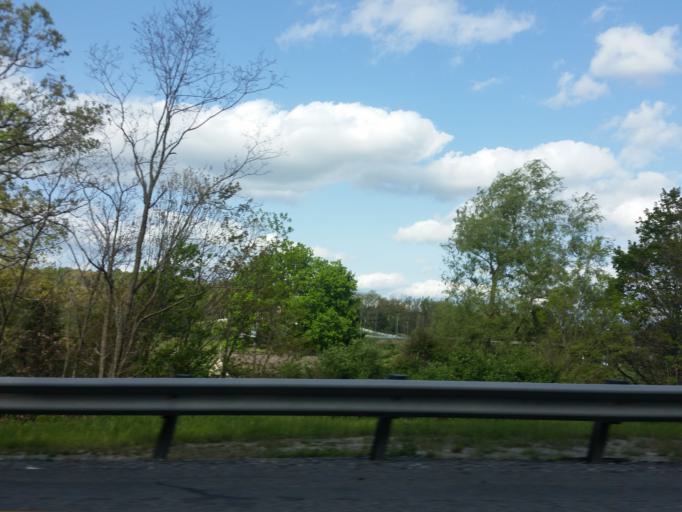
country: US
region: West Virginia
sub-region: Raleigh County
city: Shady Spring
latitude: 37.6499
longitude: -81.1119
